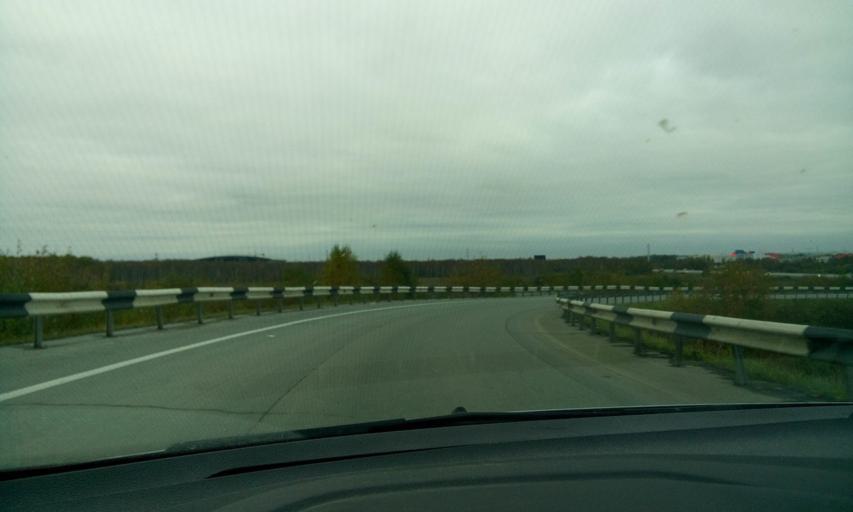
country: RU
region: Sverdlovsk
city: Istok
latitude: 56.7694
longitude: 60.7388
